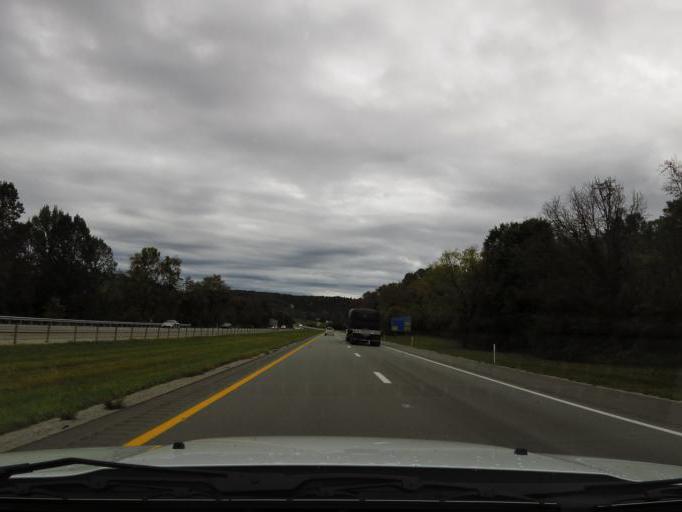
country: US
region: Kentucky
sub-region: Rockcastle County
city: Mount Vernon
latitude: 37.3518
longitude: -84.3079
